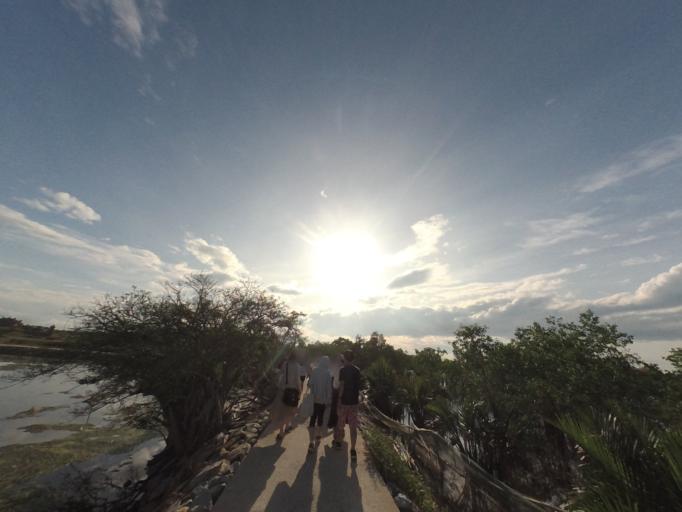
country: VN
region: Thua Thien-Hue
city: Hue
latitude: 16.5568
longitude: 107.6106
